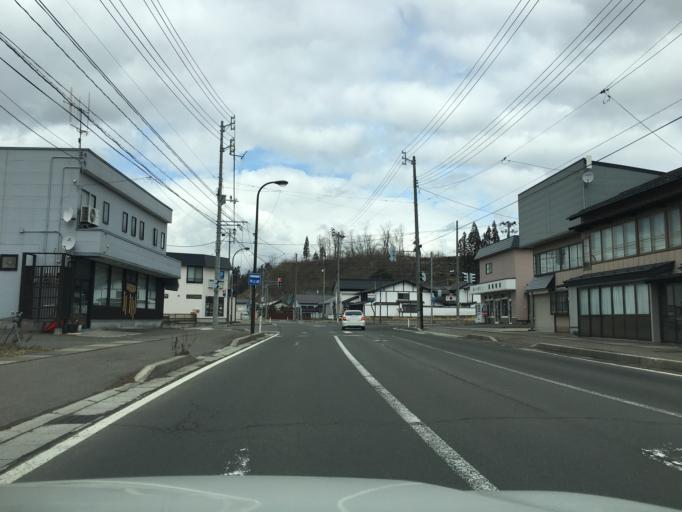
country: JP
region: Akita
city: Hanawa
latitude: 40.2734
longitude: 140.7687
